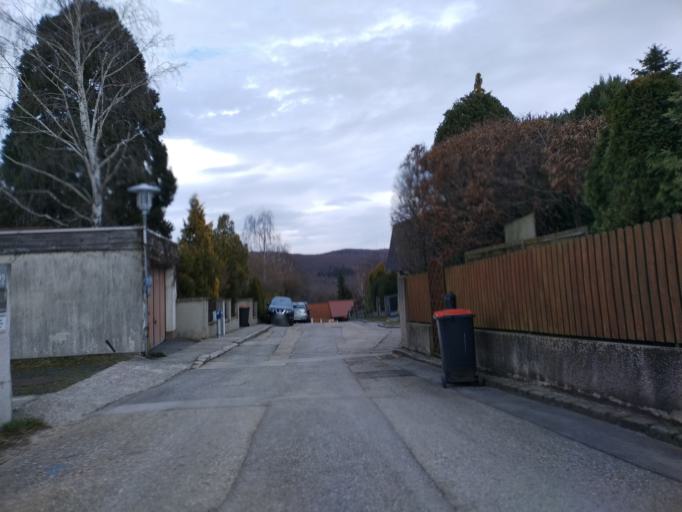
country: AT
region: Lower Austria
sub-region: Politischer Bezirk Wien-Umgebung
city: Gablitz
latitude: 48.2372
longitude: 16.1311
